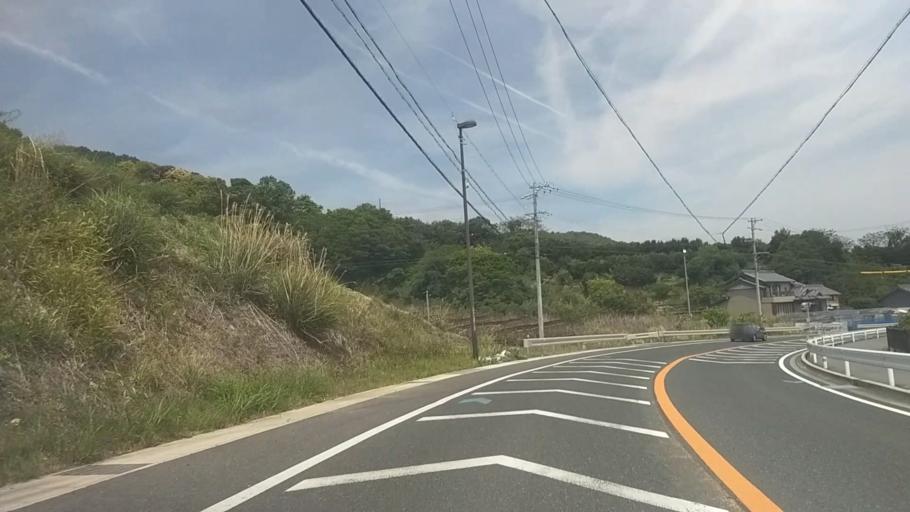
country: JP
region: Shizuoka
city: Kosai-shi
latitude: 34.7668
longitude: 137.5312
